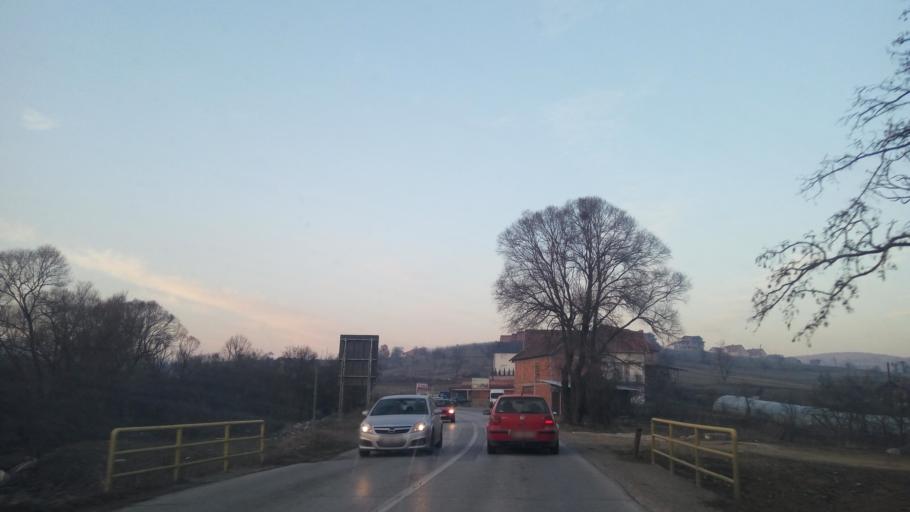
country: XK
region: Gjilan
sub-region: Komuna e Gjilanit
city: Gjilan
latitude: 42.4886
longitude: 21.3937
